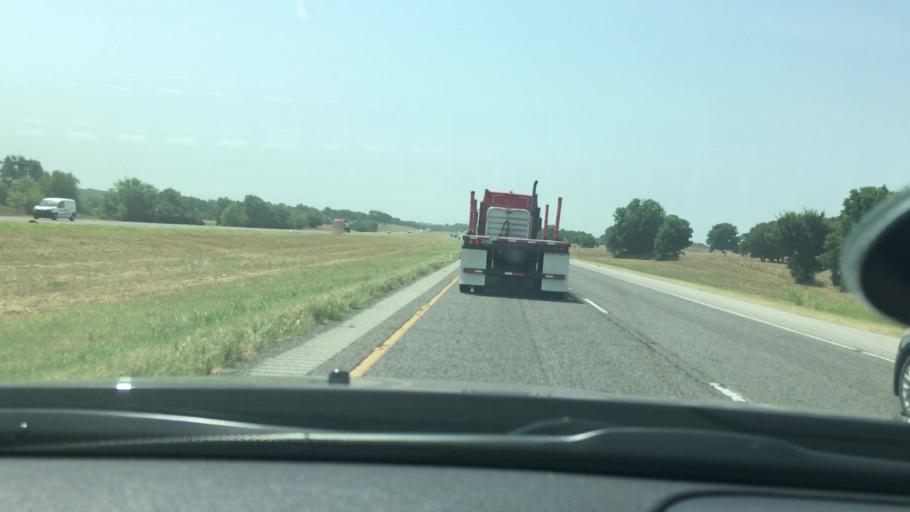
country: US
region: Oklahoma
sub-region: Garvin County
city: Wynnewood
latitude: 34.5969
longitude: -97.2093
